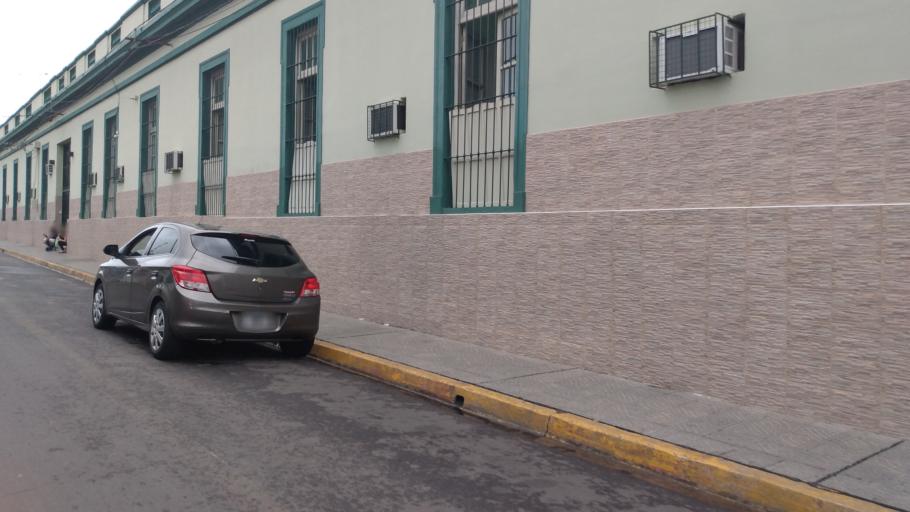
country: AR
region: Corrientes
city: Corrientes
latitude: -27.4661
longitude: -58.8414
